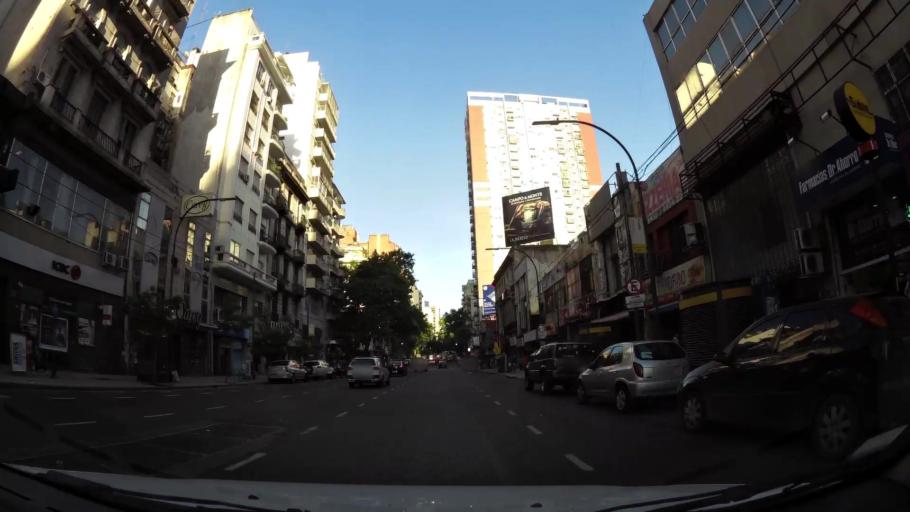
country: AR
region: Buenos Aires F.D.
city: Buenos Aires
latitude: -34.6047
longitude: -58.3991
